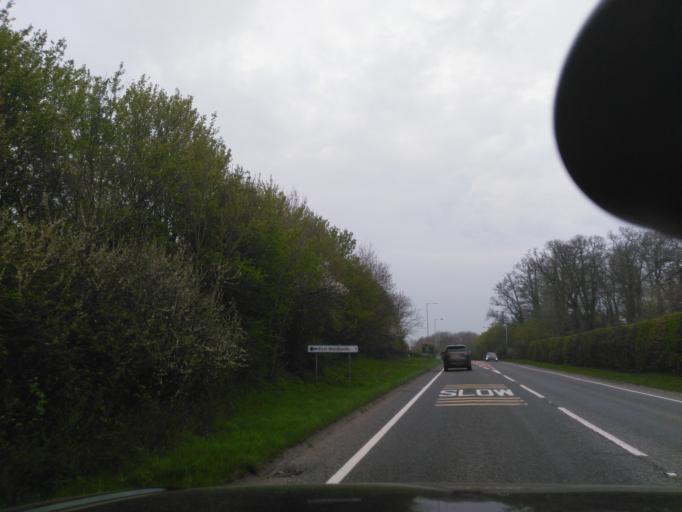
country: GB
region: England
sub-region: Somerset
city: Frome
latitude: 51.2101
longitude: -2.3141
